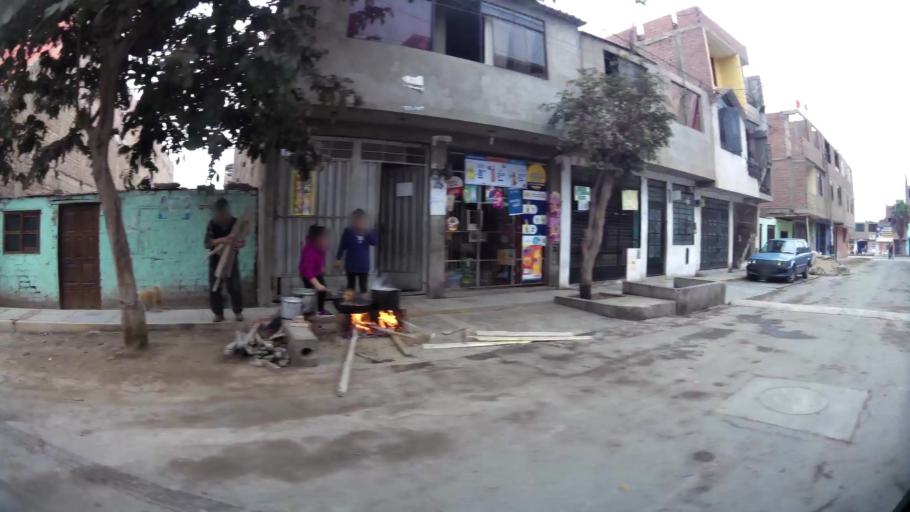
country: PE
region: Lima
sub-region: Lima
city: Independencia
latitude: -11.9664
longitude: -77.0779
